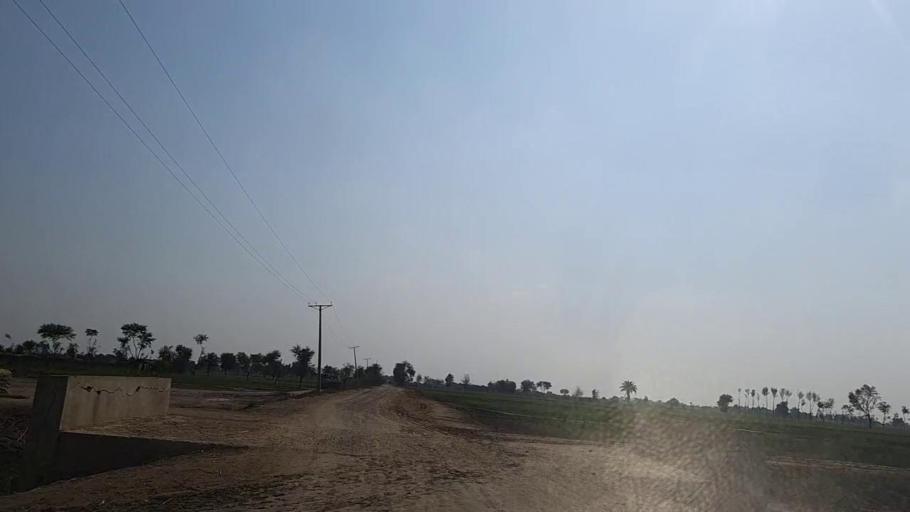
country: PK
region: Sindh
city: Daur
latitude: 26.4582
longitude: 68.2348
